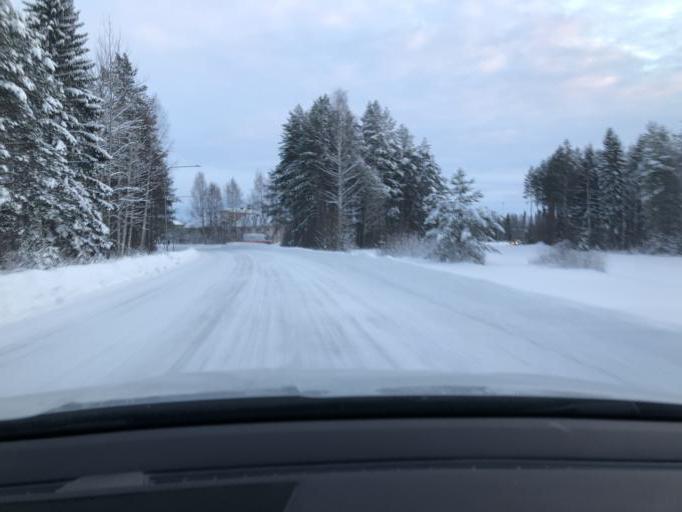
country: SE
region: Norrbotten
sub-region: Lulea Kommun
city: Bergnaset
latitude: 65.6186
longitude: 22.1196
